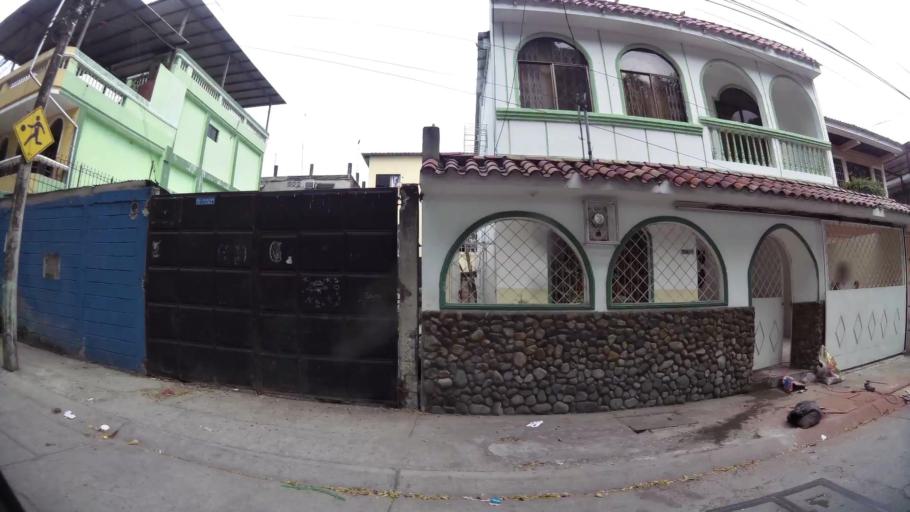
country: EC
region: Guayas
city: Eloy Alfaro
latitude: -2.1201
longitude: -79.8955
